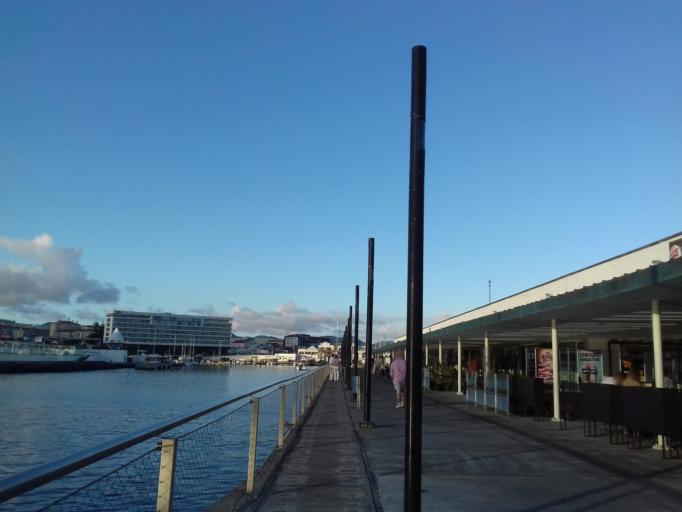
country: PT
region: Azores
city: Ponta Delgada
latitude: 37.7388
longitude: -25.6616
